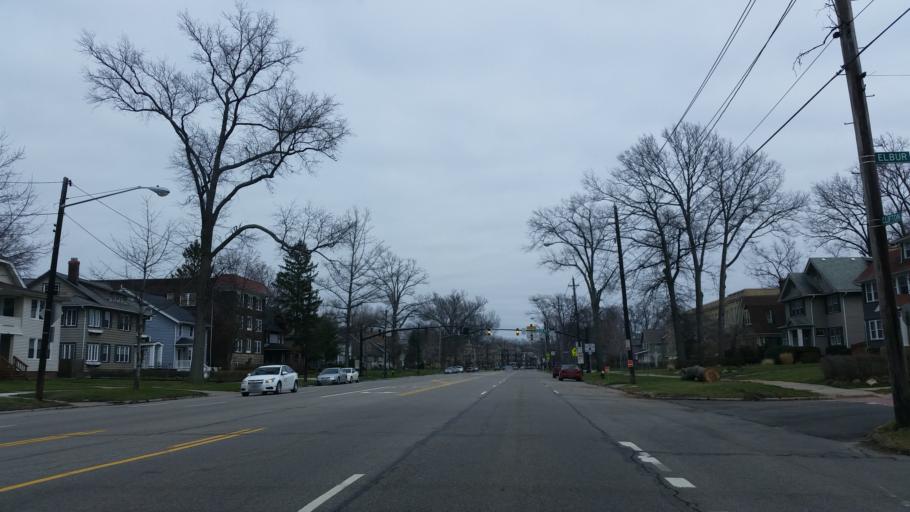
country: US
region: Ohio
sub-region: Cuyahoga County
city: Lakewood
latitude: 41.4910
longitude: -81.7867
